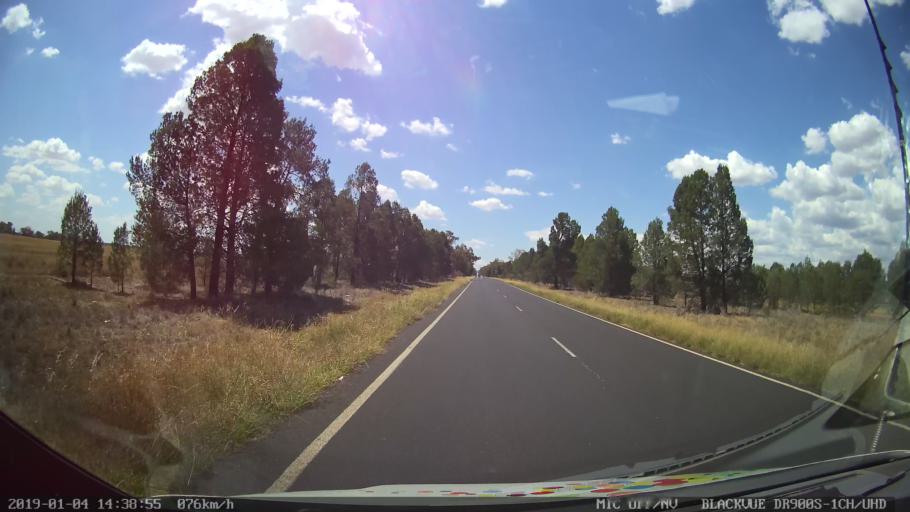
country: AU
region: New South Wales
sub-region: Dubbo Municipality
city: Dubbo
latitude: -32.1708
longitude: 148.6319
